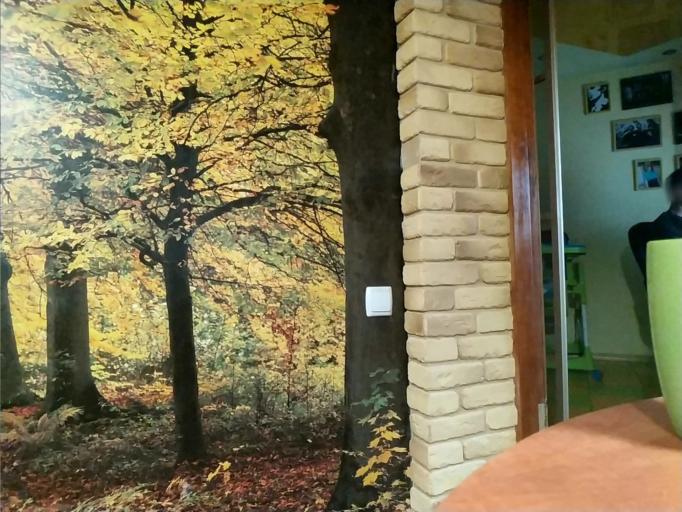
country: RU
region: Tverskaya
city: Staraya Toropa
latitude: 56.3408
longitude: 31.8513
